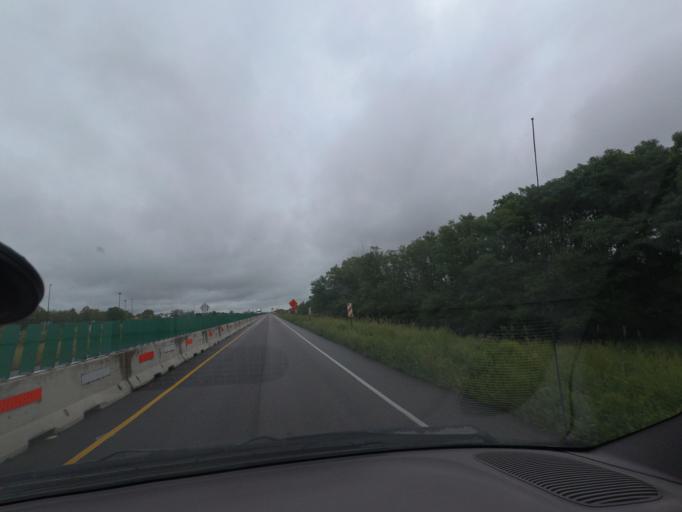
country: US
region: Illinois
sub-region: Piatt County
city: Cerro Gordo
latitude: 39.9856
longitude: -88.7879
